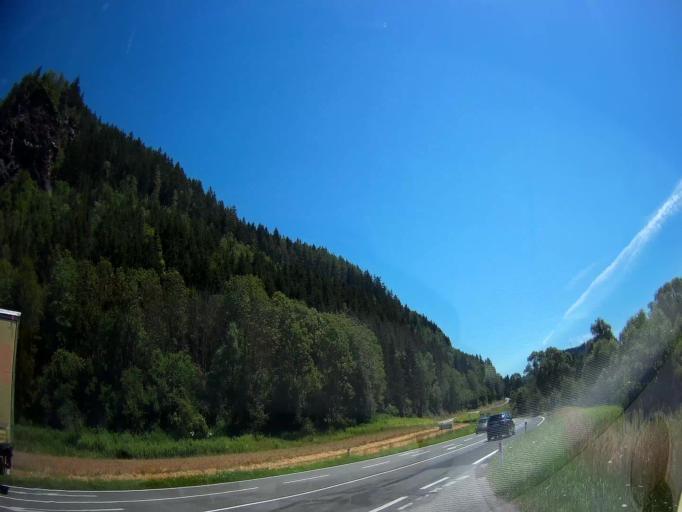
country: AT
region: Carinthia
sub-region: Politischer Bezirk Sankt Veit an der Glan
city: Micheldorf
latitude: 46.9009
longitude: 14.4399
